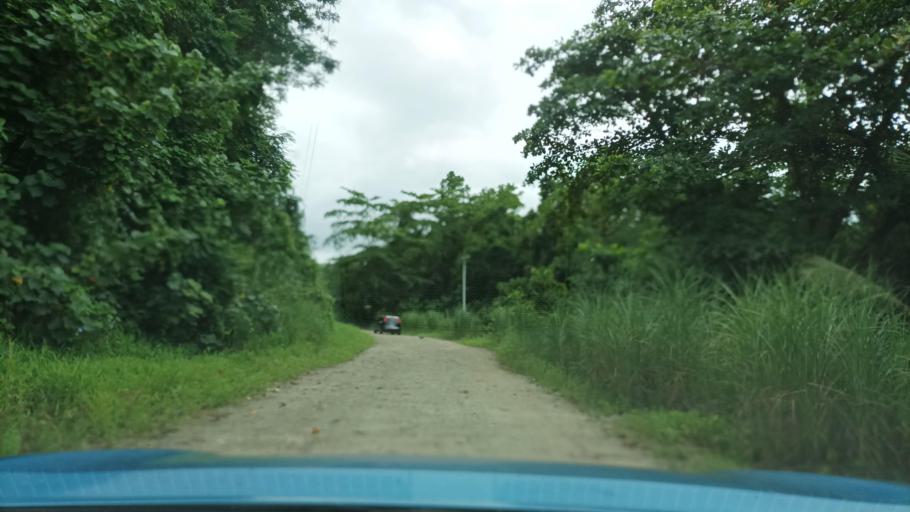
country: FM
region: Pohnpei
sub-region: Kolonia Municipality
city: Kolonia
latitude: 6.9764
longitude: 158.2230
